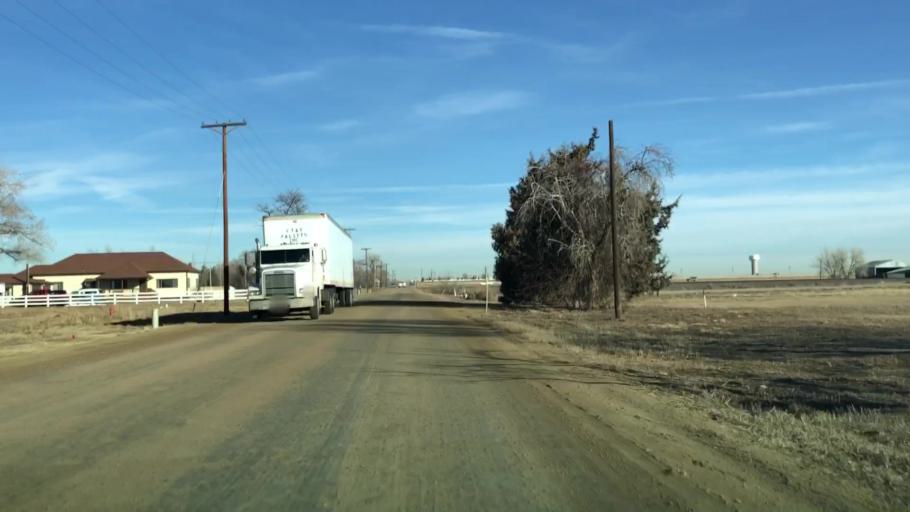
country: US
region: Colorado
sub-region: Weld County
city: Johnstown
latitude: 40.4044
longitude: -104.9643
